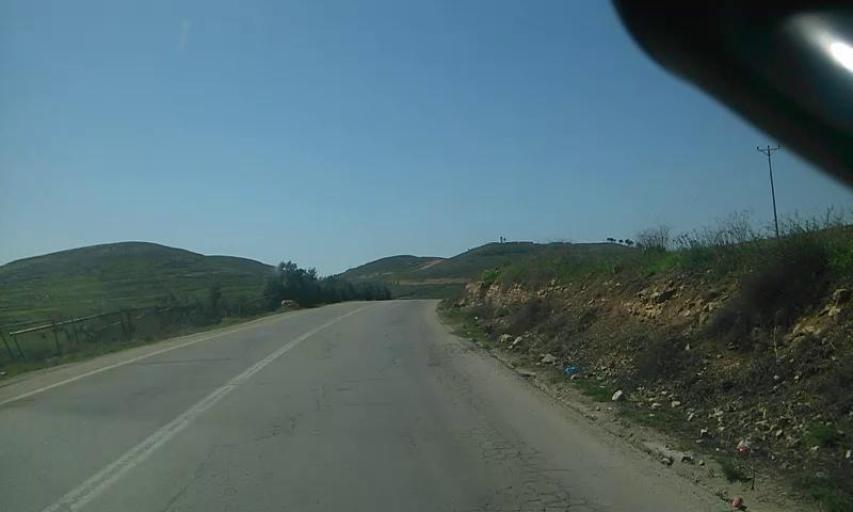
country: PS
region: West Bank
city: Ar Rihiyah
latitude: 31.4842
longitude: 35.0510
